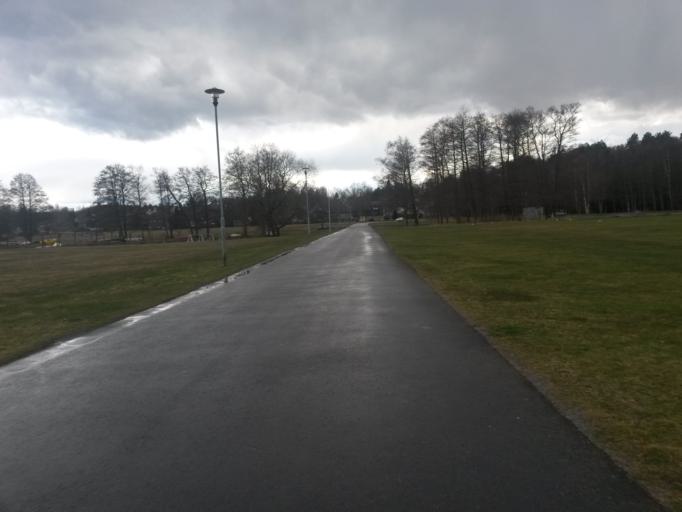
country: SE
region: OErebro
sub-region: Karlskoga Kommun
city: Karlskoga
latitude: 59.3168
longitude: 14.5154
